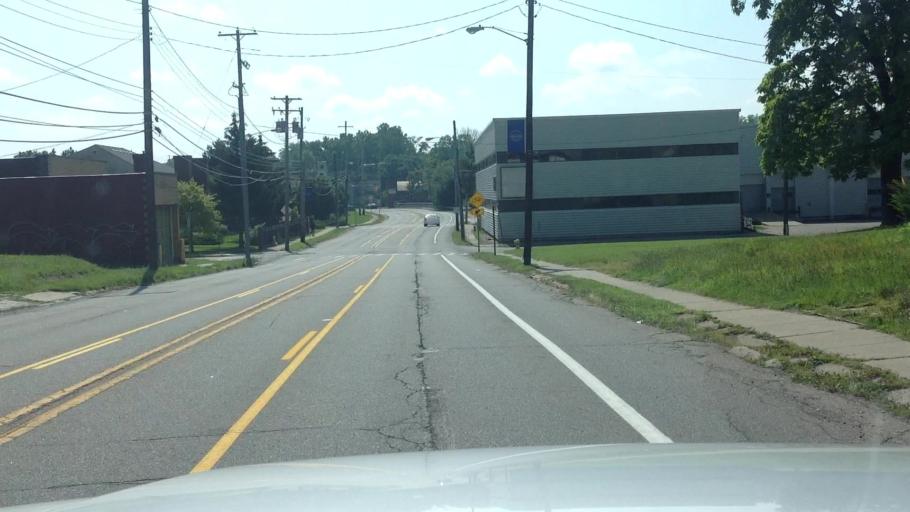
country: US
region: Michigan
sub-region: Genesee County
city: Flint
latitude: 43.0171
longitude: -83.6982
